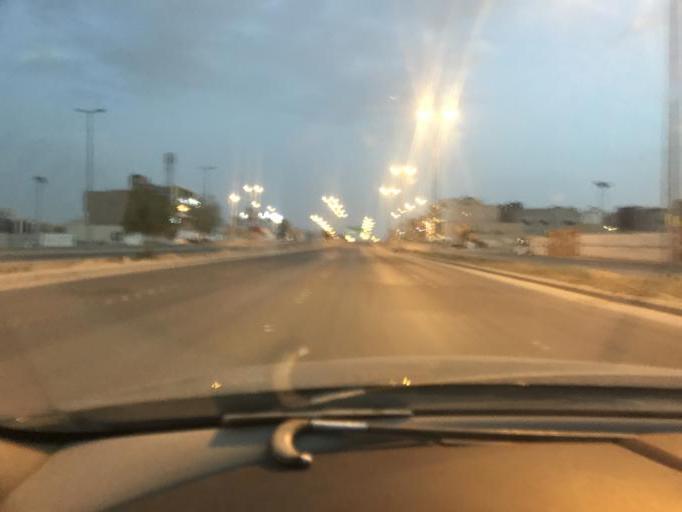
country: SA
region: Ar Riyad
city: Riyadh
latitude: 24.8431
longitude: 46.6750
